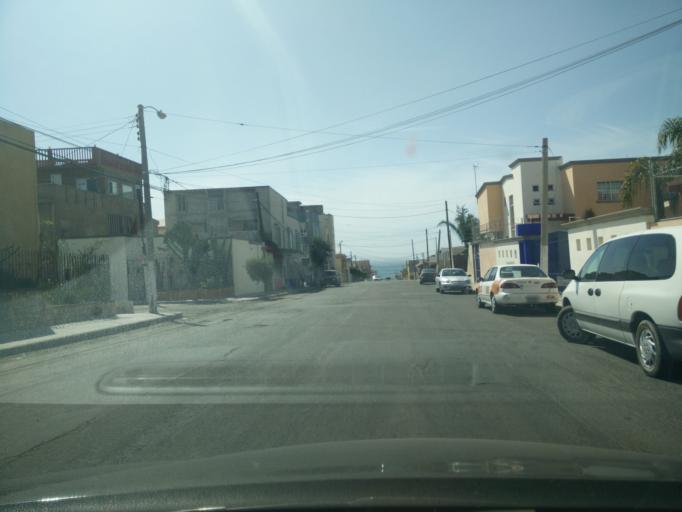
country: MX
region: Baja California
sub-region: Tijuana
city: La Esperanza [Granjas Familiares]
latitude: 32.5137
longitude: -117.1177
